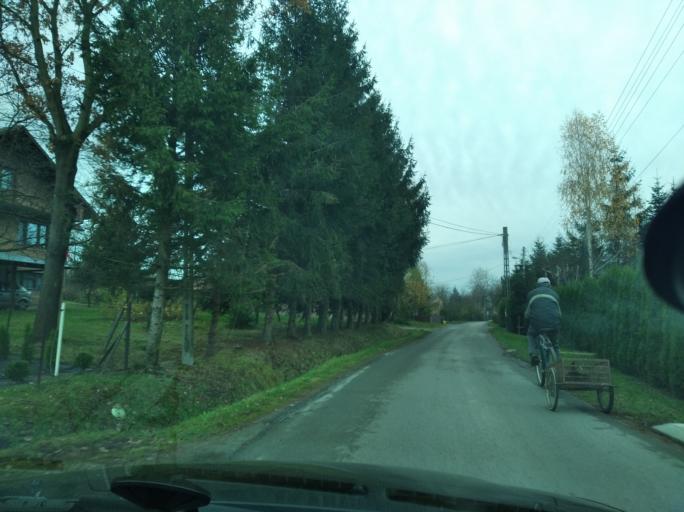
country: PL
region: Subcarpathian Voivodeship
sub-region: Powiat lancucki
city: Markowa
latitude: 50.0218
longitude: 22.3230
